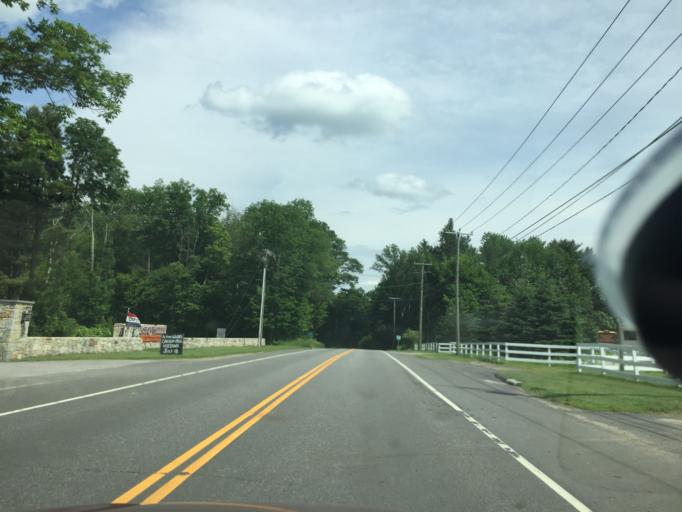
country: US
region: Connecticut
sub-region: Litchfield County
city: West Torrington
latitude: 41.8299
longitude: -73.1912
